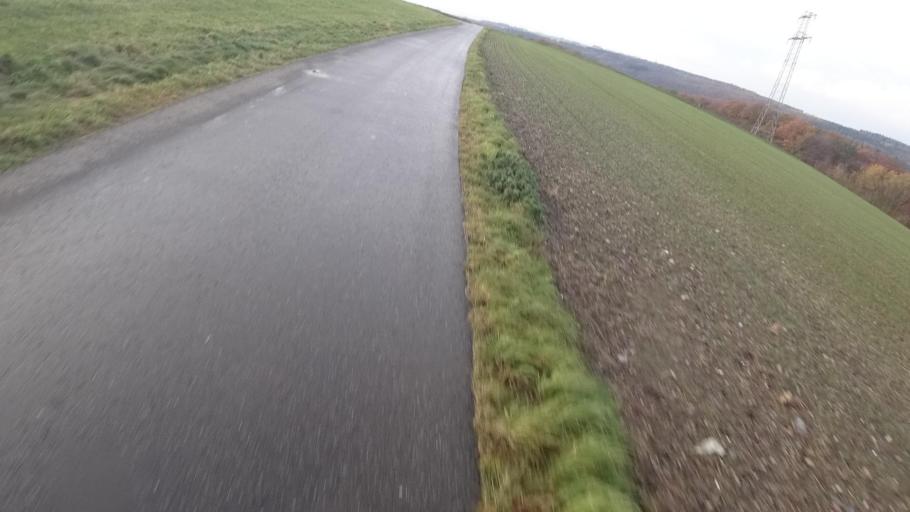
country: DE
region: Rheinland-Pfalz
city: Bickenbach
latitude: 50.1289
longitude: 7.5157
